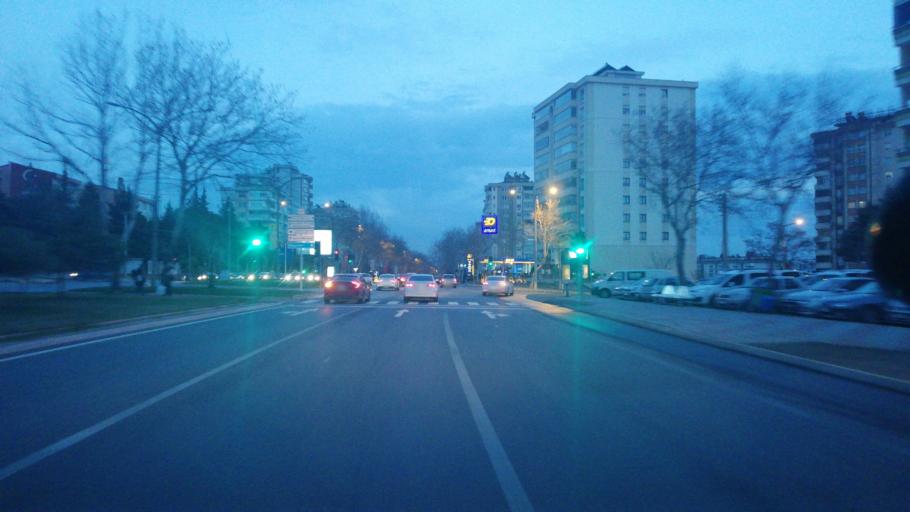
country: TR
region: Kahramanmaras
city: Kahramanmaras
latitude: 37.5885
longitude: 36.8863
